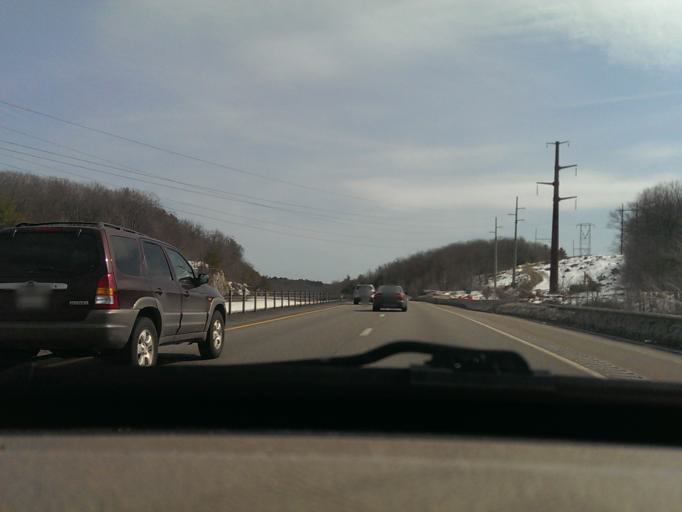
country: US
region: Massachusetts
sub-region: Worcester County
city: Sutton
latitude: 42.1405
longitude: -71.7132
